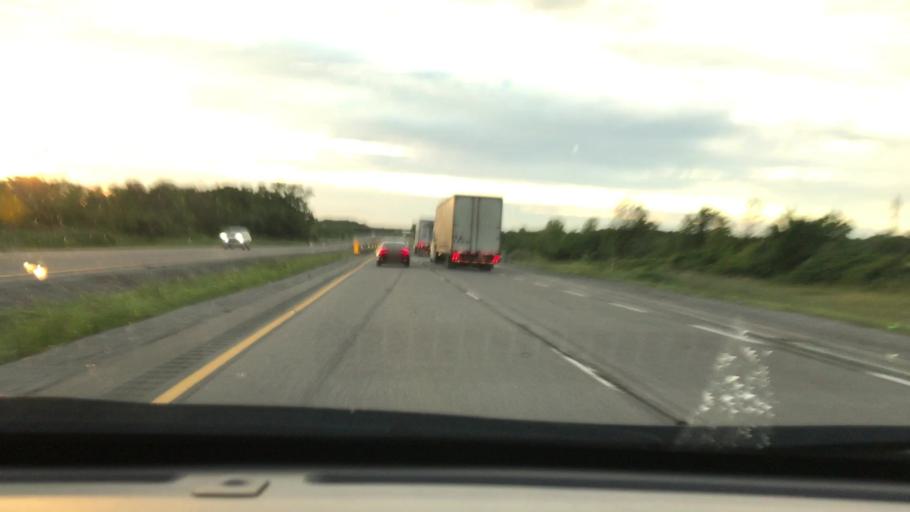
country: CA
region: Ontario
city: Niagara Falls
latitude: 43.0264
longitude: -79.1043
